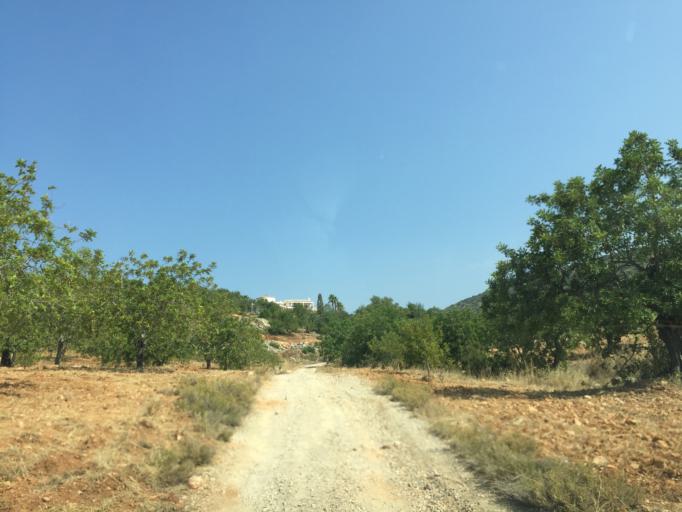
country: PT
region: Faro
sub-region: Loule
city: Almancil
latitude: 37.1033
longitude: -8.0052
